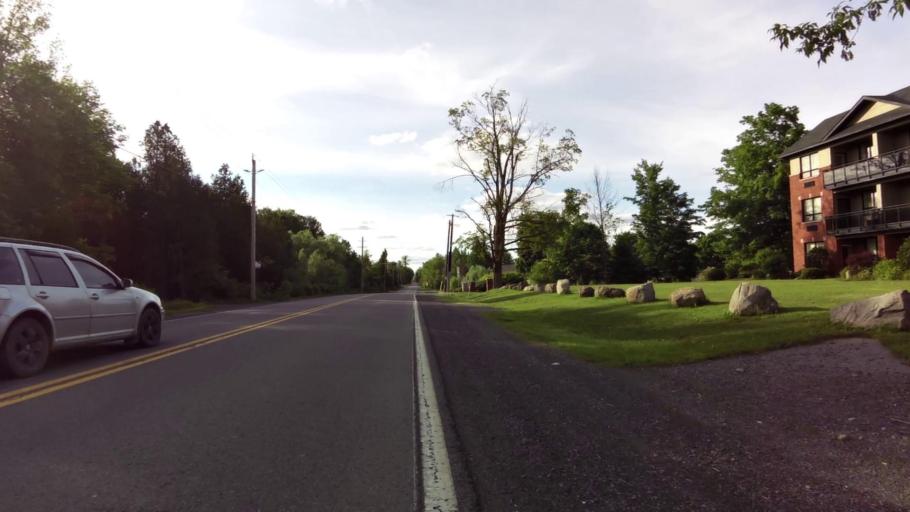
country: CA
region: Ontario
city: Ottawa
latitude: 45.2350
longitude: -75.6113
